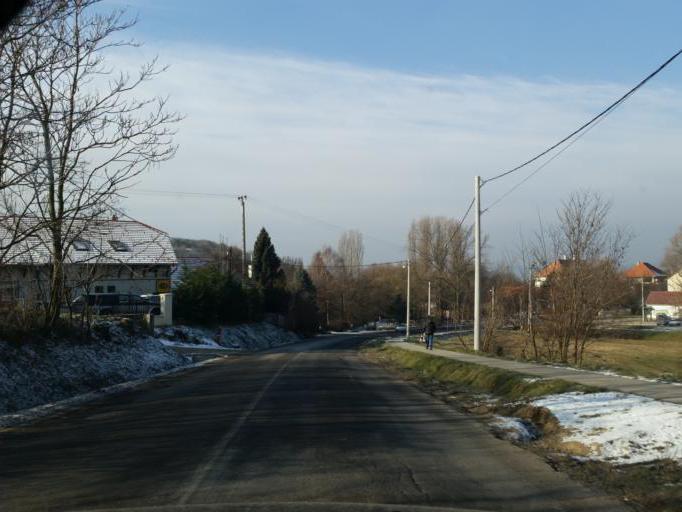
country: HU
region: Pest
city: Telki
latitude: 47.5536
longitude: 18.8072
